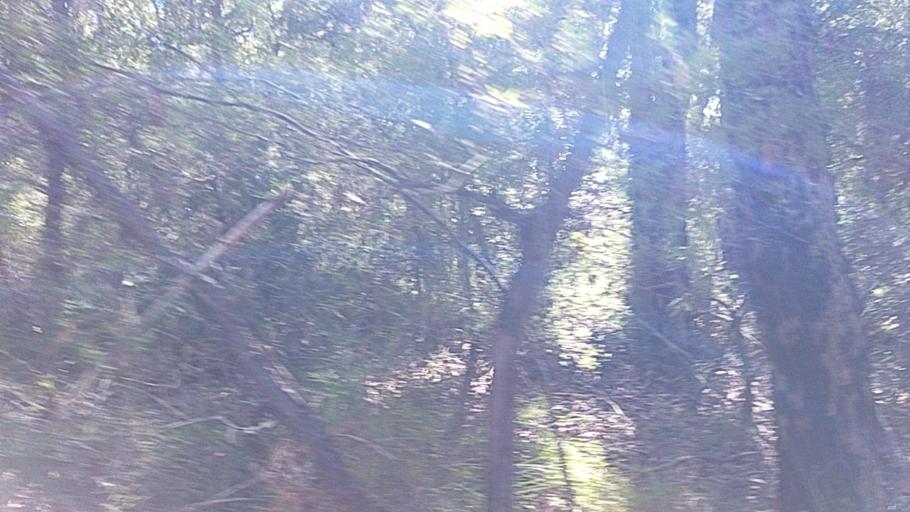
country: AU
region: New South Wales
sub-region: Ryde
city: East Ryde
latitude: -33.8147
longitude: 151.1315
